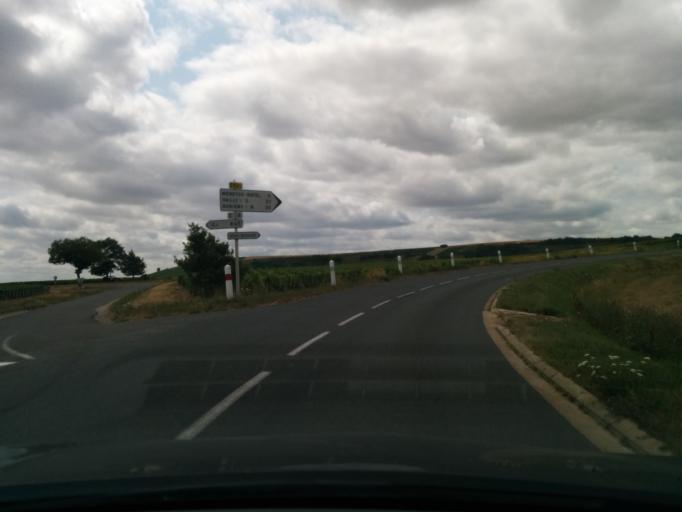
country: FR
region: Centre
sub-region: Departement du Cher
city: Sancerre
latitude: 47.3155
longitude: 2.7998
